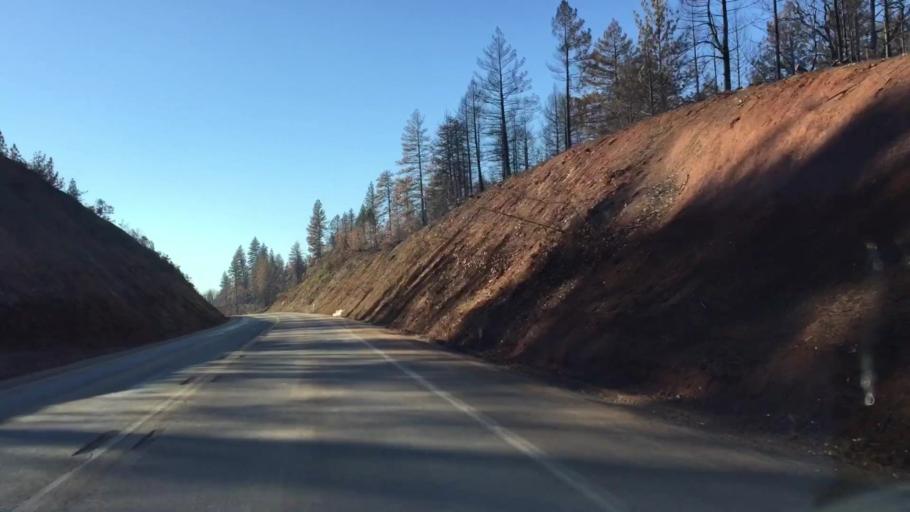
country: US
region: California
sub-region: Butte County
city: Magalia
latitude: 39.7223
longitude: -121.5117
